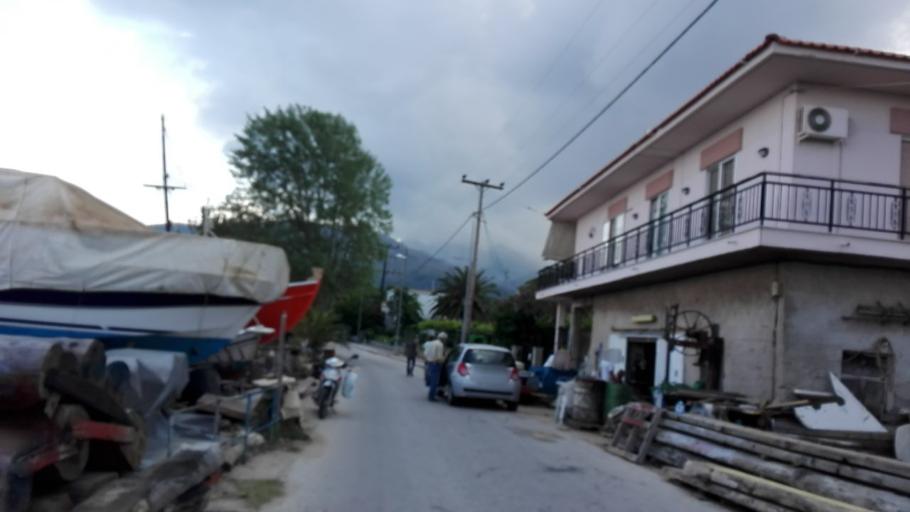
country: GR
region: East Macedonia and Thrace
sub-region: Nomos Kavalas
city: Prinos
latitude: 40.7591
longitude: 24.5739
